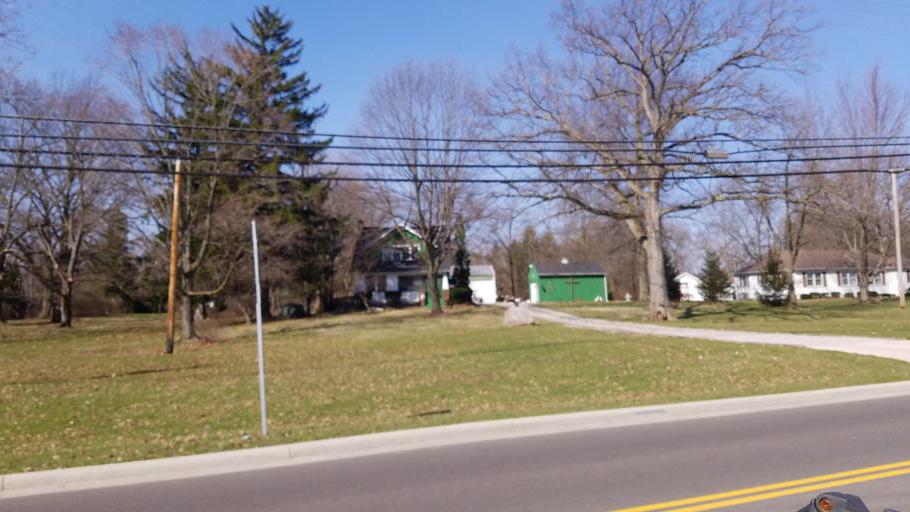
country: US
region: Ohio
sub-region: Marion County
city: Marion
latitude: 40.5720
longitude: -83.0927
